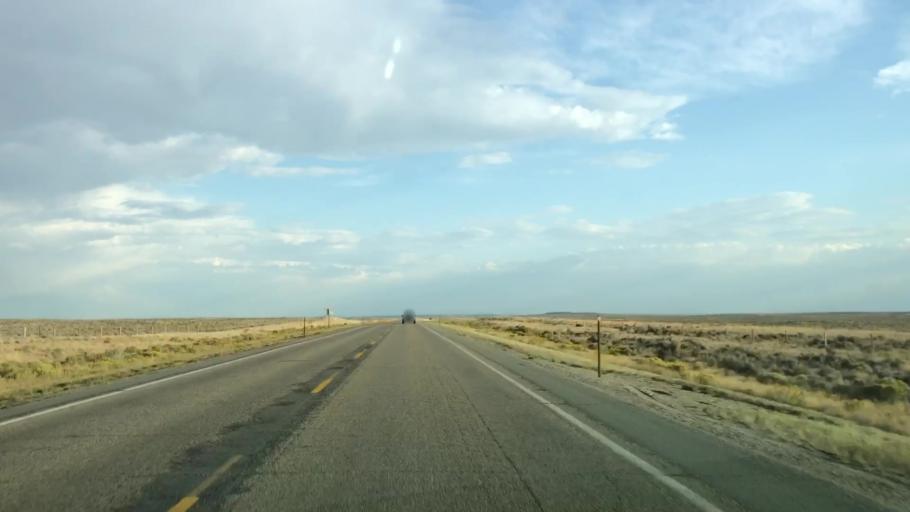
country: US
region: Wyoming
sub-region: Sublette County
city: Pinedale
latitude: 42.4081
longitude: -109.5509
